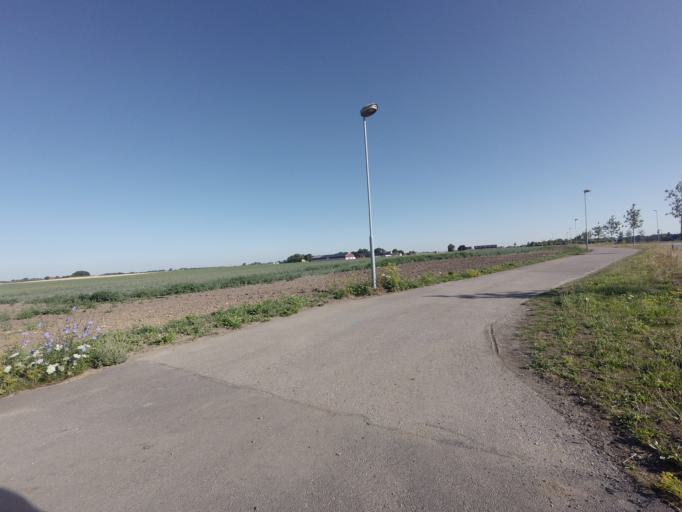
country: SE
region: Skane
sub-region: Trelleborgs Kommun
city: Trelleborg
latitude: 55.3869
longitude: 13.1106
